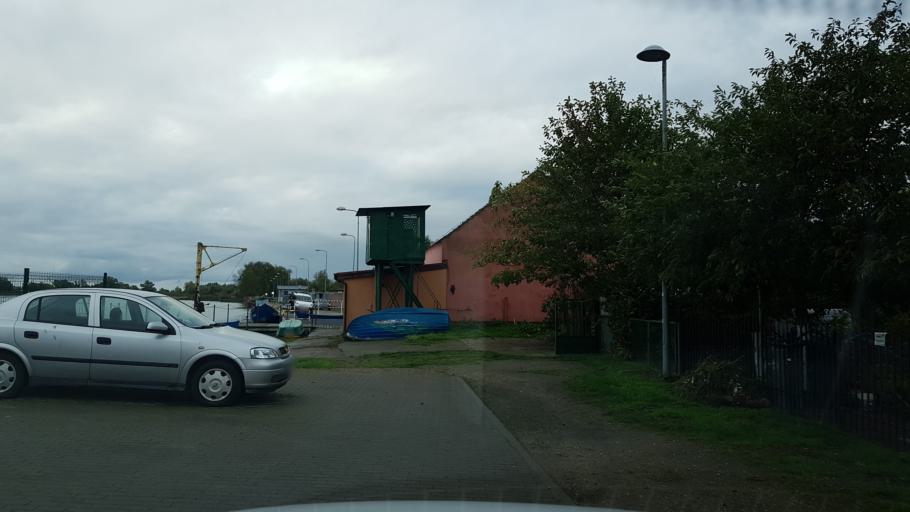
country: PL
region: West Pomeranian Voivodeship
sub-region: Powiat kamienski
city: Wolin
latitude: 53.8399
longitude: 14.6165
